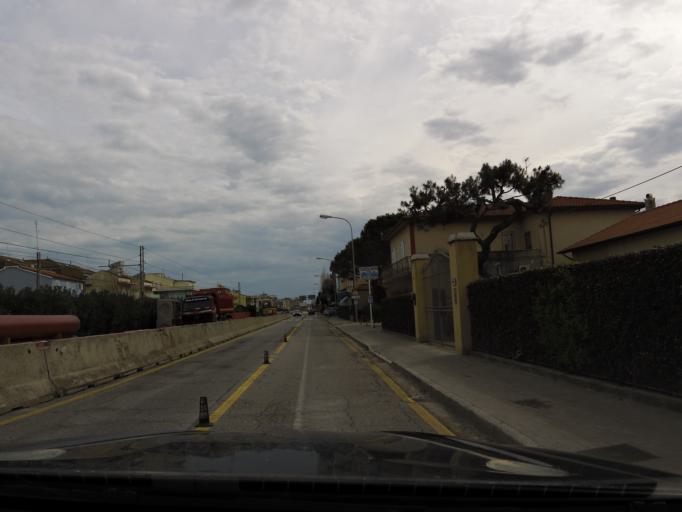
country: IT
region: The Marches
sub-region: Provincia di Macerata
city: Civitanova Marche
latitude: 43.3197
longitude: 13.7198
